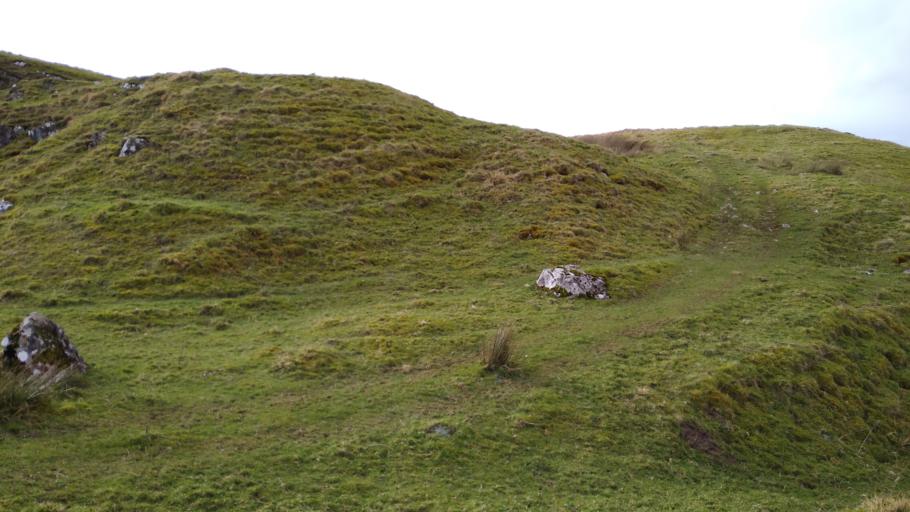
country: GB
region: England
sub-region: Cumbria
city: Wigton
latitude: 54.7329
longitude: -3.1381
